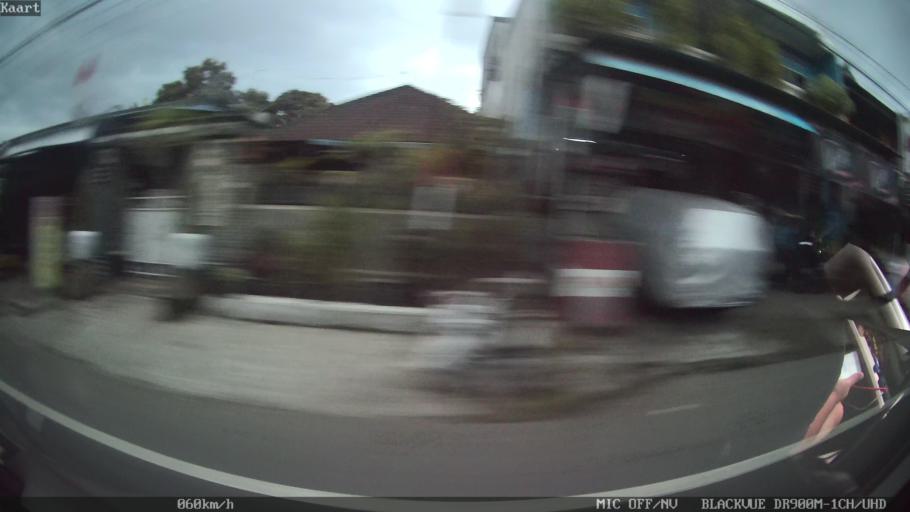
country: ID
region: Bali
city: Banjar Meliling Kawan
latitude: -8.5095
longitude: 115.0807
